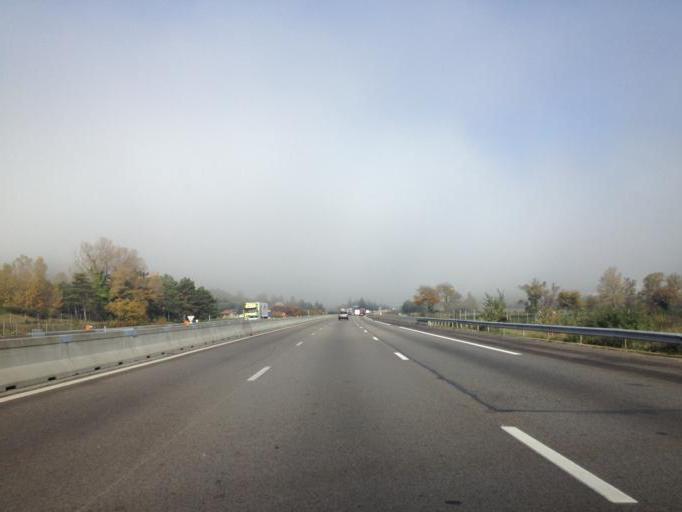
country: FR
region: Rhone-Alpes
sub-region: Departement de la Drome
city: Saint-Marcel-les-Sauzet
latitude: 44.5960
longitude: 4.7976
